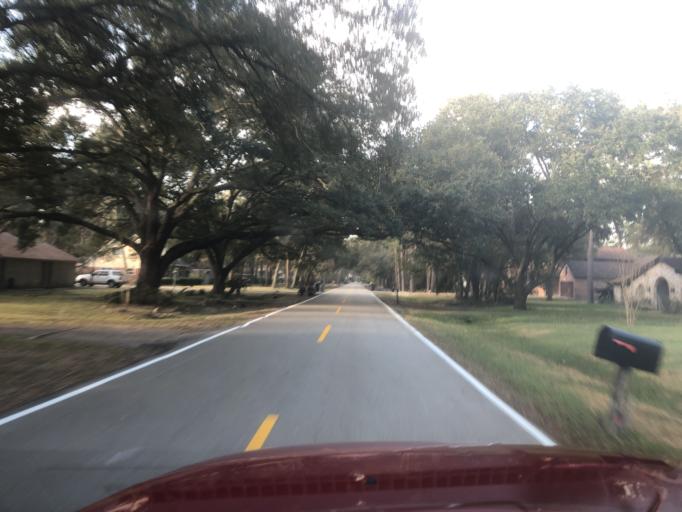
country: US
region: Texas
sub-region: Harris County
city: Spring
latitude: 30.0209
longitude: -95.4745
